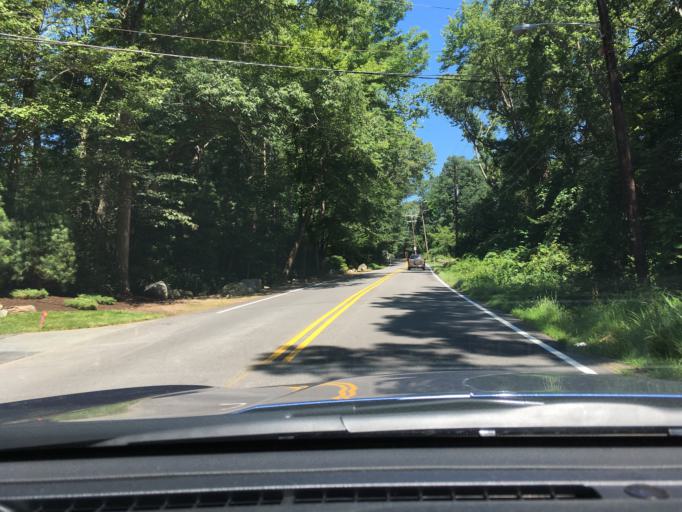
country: US
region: Rhode Island
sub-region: Kent County
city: East Greenwich
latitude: 41.6572
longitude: -71.4764
